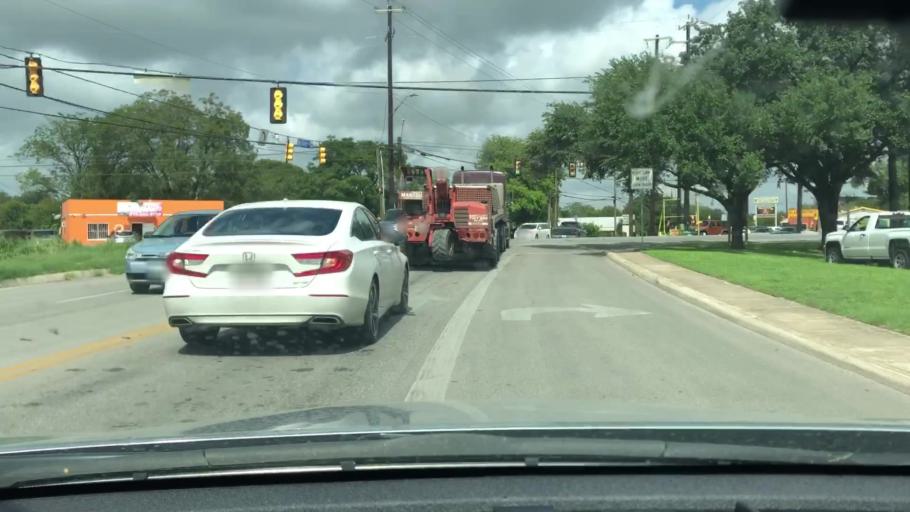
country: US
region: Texas
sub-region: Bexar County
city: Windcrest
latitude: 29.5327
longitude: -98.3789
